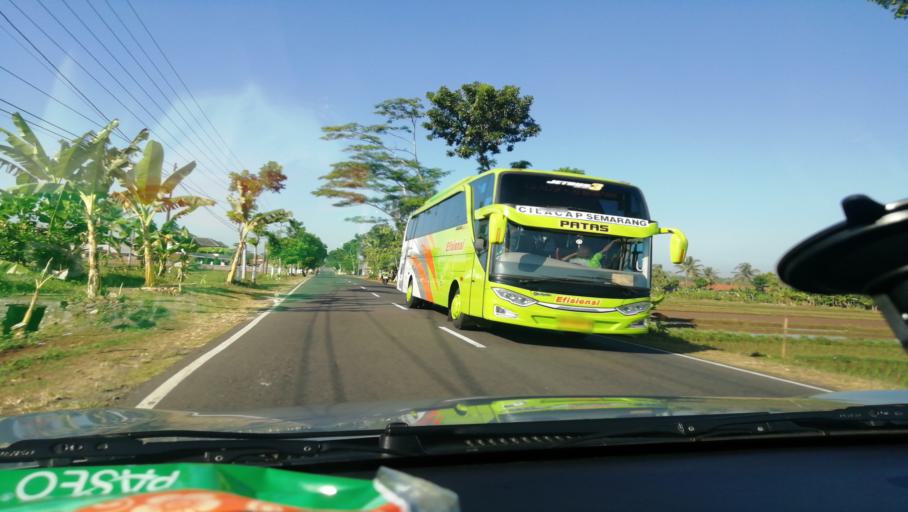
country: ID
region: Central Java
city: Kutoarjo
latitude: -7.7181
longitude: 109.9731
